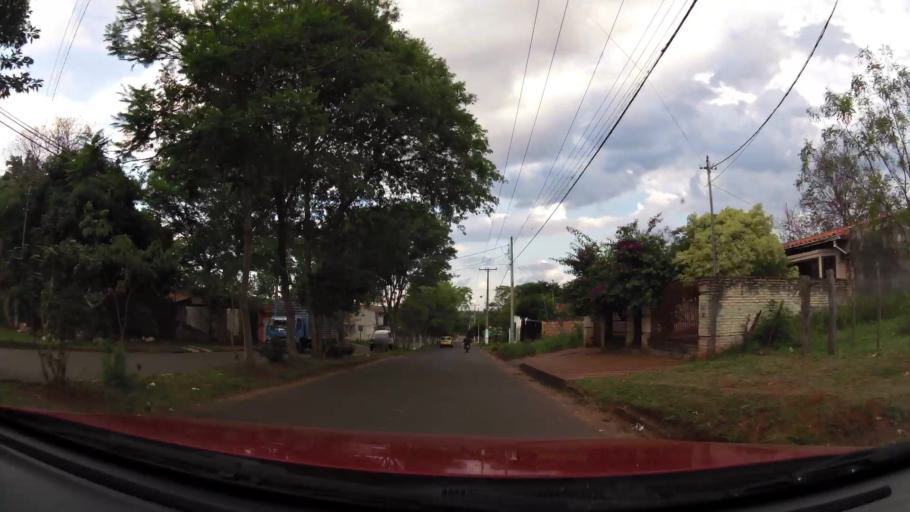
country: PY
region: Central
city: Nemby
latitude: -25.3708
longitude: -57.5515
